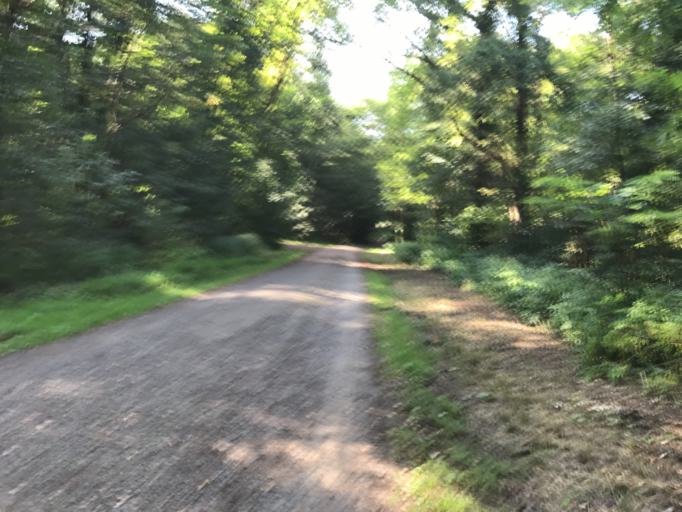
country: DE
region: Rheinland-Pfalz
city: Budenheim
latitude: 50.0148
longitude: 8.1856
